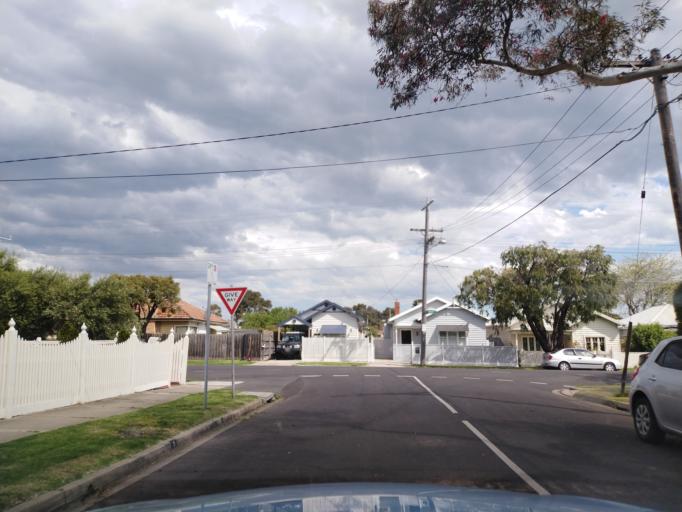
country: AU
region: Victoria
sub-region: Hobsons Bay
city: Newport
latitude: -37.8457
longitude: 144.8793
